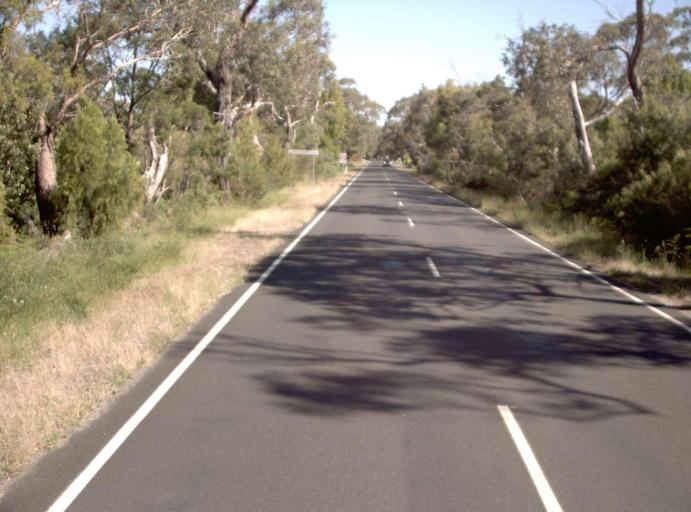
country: AU
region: Victoria
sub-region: Latrobe
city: Traralgon
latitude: -38.6496
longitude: 146.6745
